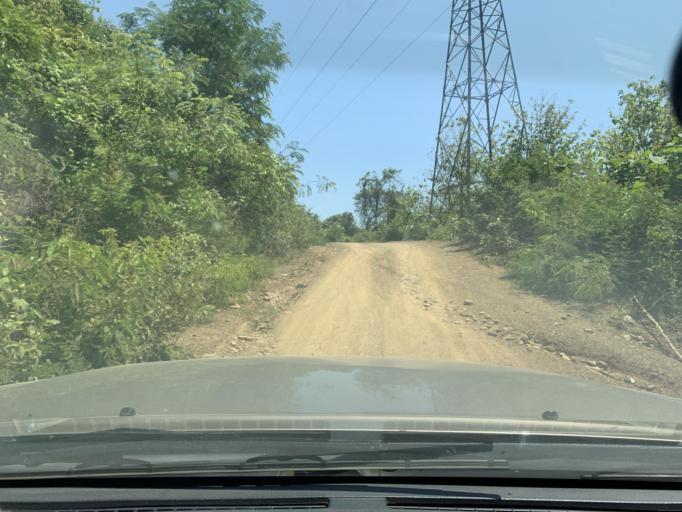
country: LA
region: Louangphabang
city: Louangphabang
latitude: 19.9032
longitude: 102.2187
